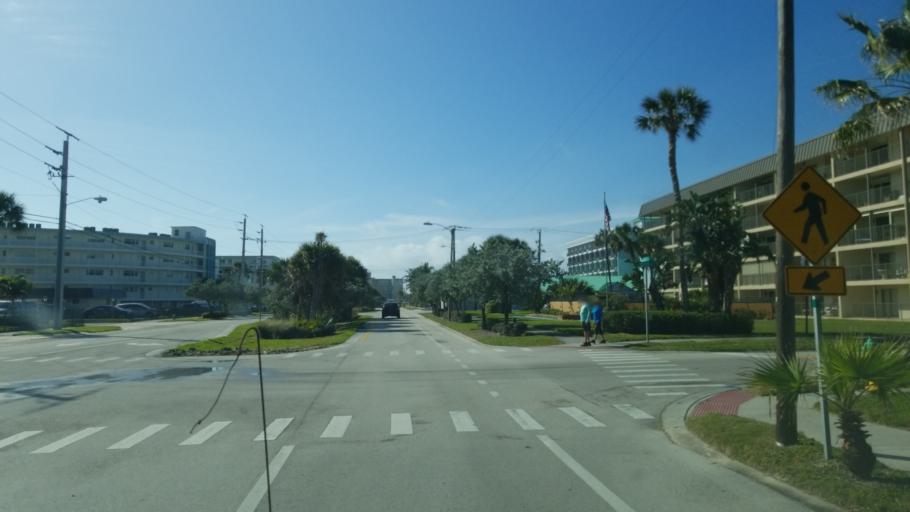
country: US
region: Florida
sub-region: Brevard County
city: Cocoa Beach
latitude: 28.3559
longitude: -80.6059
